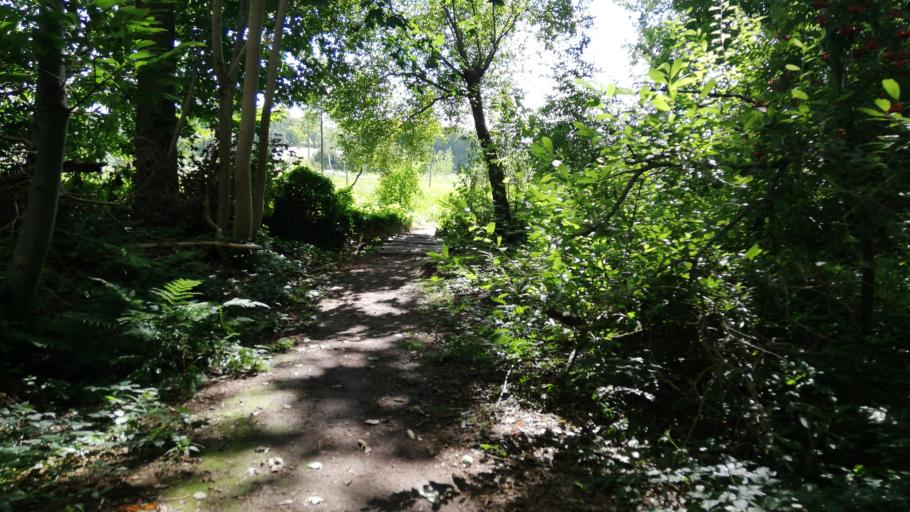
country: BE
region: Flanders
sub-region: Provincie West-Vlaanderen
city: Jabbeke
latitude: 51.1701
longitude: 3.0842
